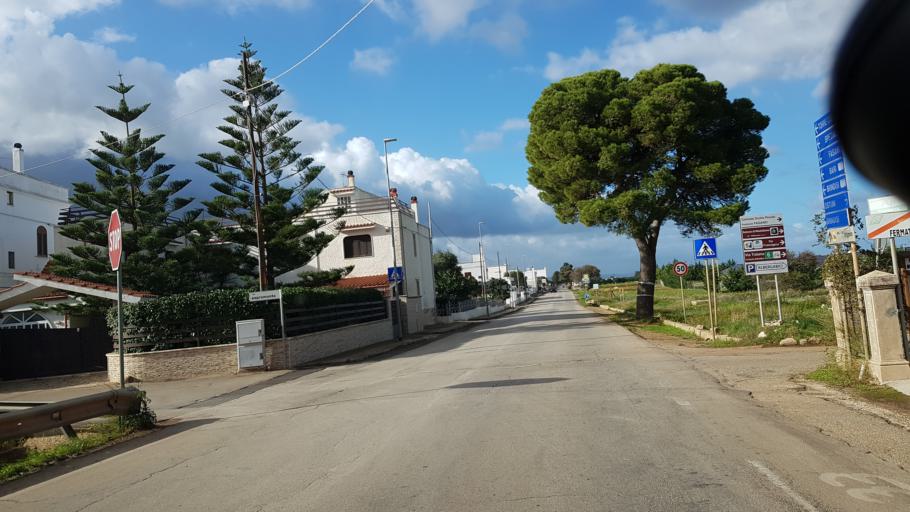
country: IT
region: Apulia
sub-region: Provincia di Brindisi
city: Montalbano
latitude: 40.7808
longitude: 17.4839
